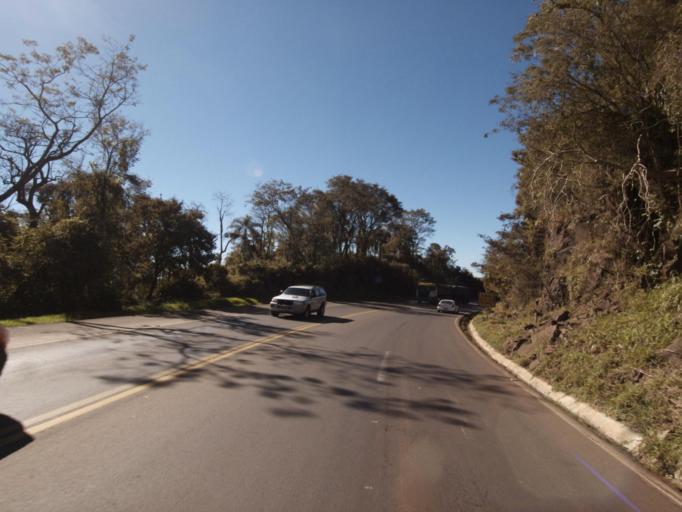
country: BR
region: Santa Catarina
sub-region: Chapeco
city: Chapeco
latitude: -26.9843
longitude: -52.6038
